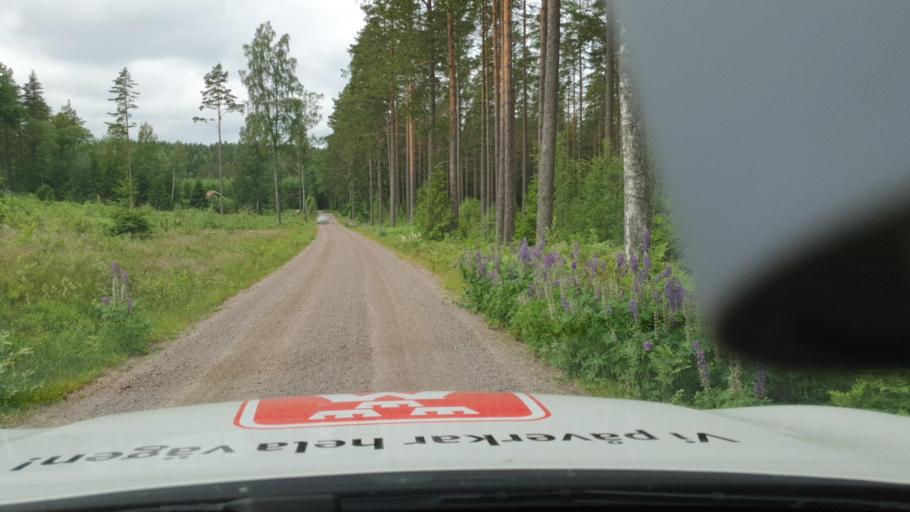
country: SE
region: Vaestra Goetaland
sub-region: Hjo Kommun
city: Hjo
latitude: 58.3985
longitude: 14.3363
